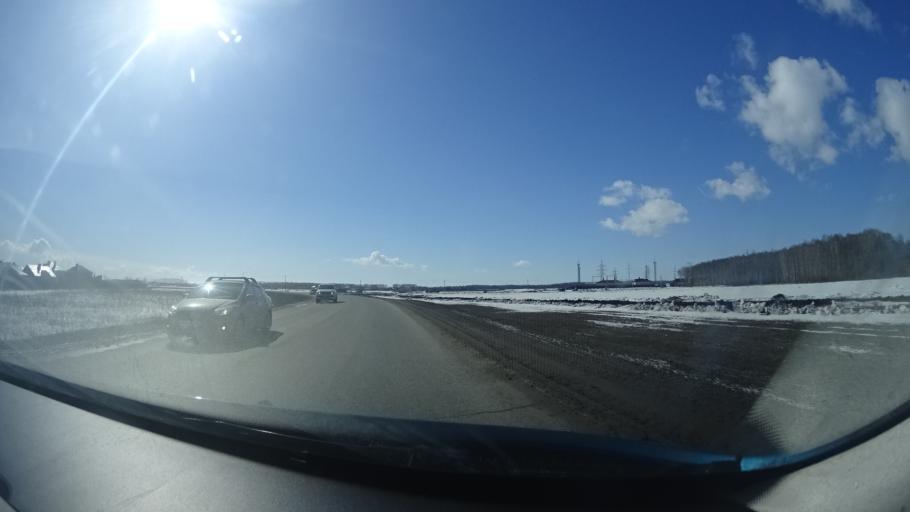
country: RU
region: Bashkortostan
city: Ufa
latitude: 54.6284
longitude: 55.8954
